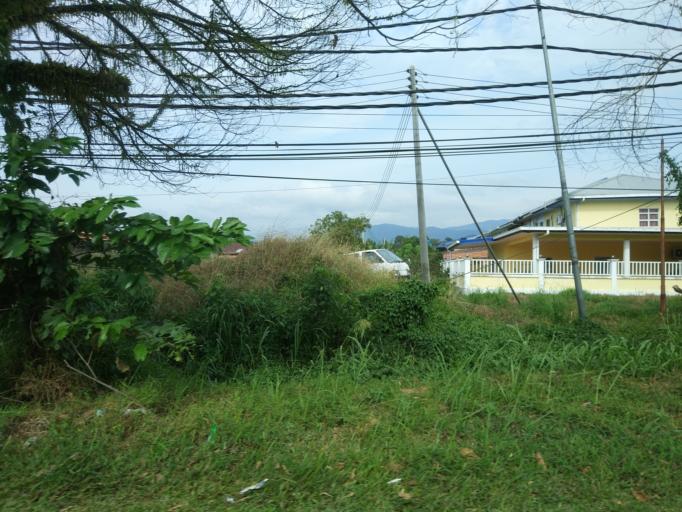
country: MY
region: Sabah
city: Beaufort
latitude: 5.0646
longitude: 115.5503
